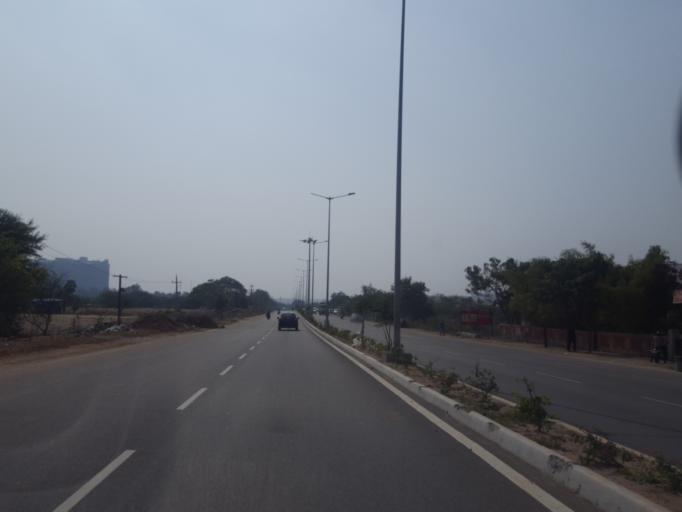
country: IN
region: Telangana
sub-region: Medak
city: Serilingampalle
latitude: 17.4151
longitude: 78.3338
